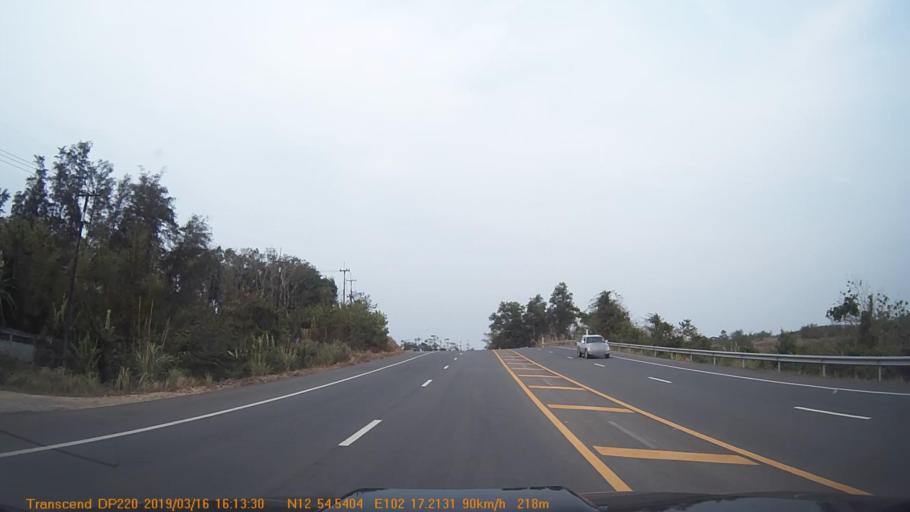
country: TH
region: Chanthaburi
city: Pong Nam Ron
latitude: 12.9092
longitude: 102.2871
